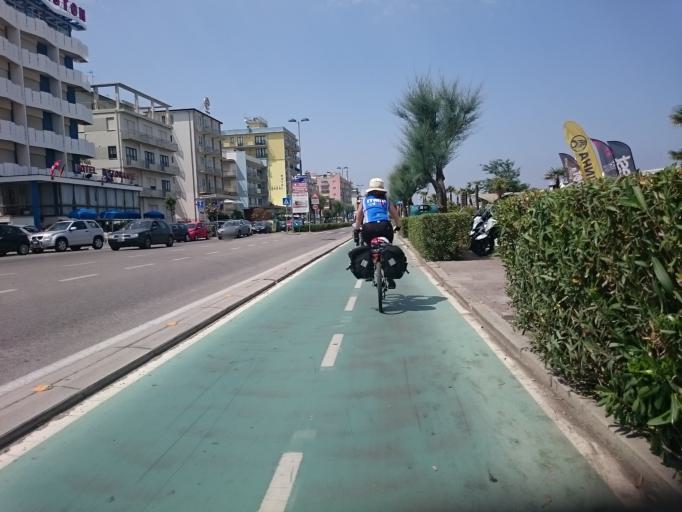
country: IT
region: Veneto
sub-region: Provincia di Venezia
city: Chioggia
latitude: 45.2128
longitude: 12.2953
